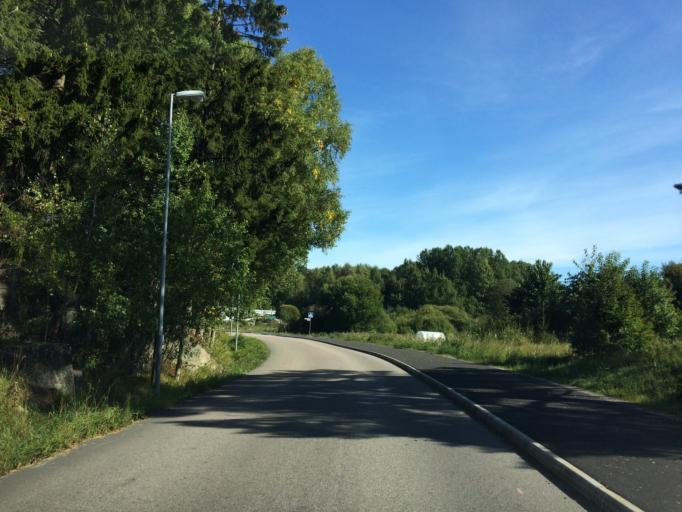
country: SE
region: Stockholm
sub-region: Stockholms Kommun
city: Kista
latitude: 59.4056
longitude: 17.9829
